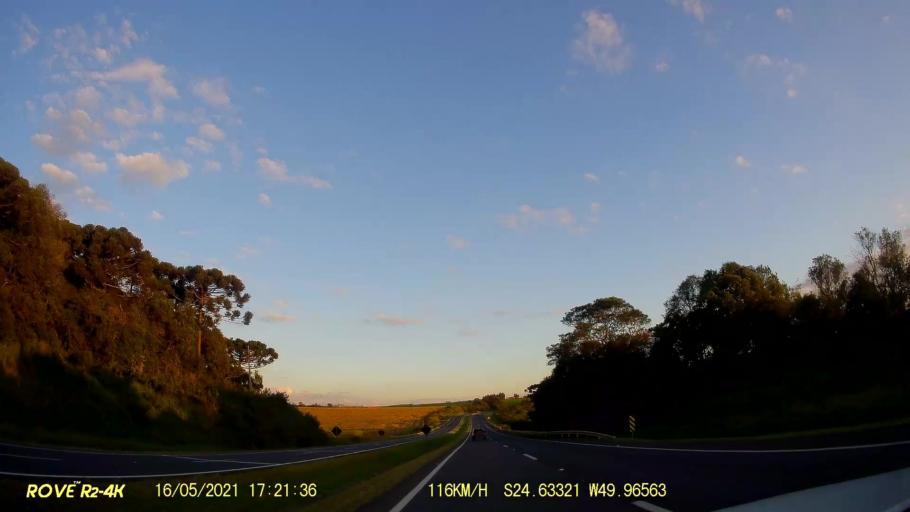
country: BR
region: Parana
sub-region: Pirai Do Sul
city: Pirai do Sul
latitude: -24.6338
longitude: -49.9657
